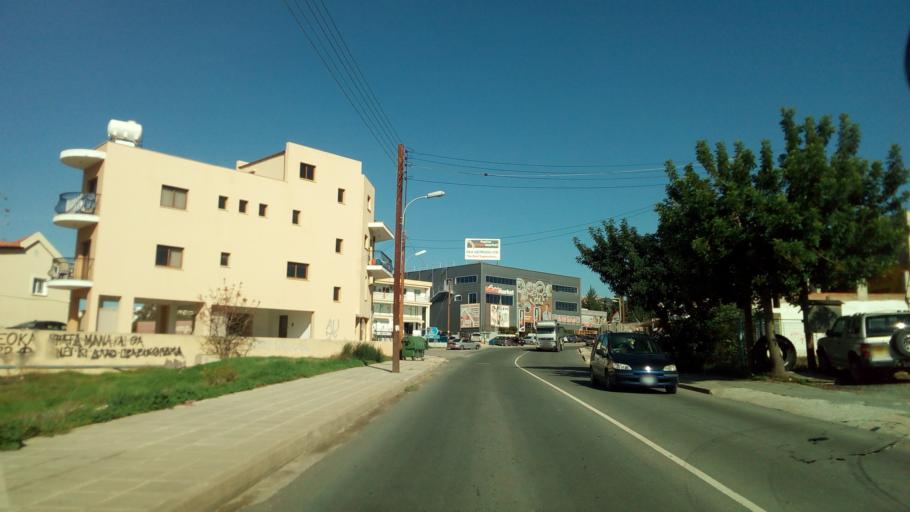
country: CY
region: Pafos
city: Mesogi
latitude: 34.7971
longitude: 32.4465
